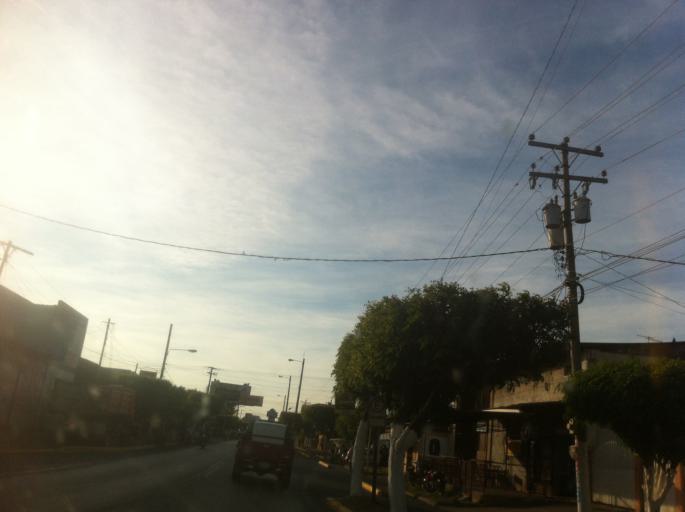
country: NI
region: Rivas
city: Rivas
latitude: 11.4254
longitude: -85.8052
